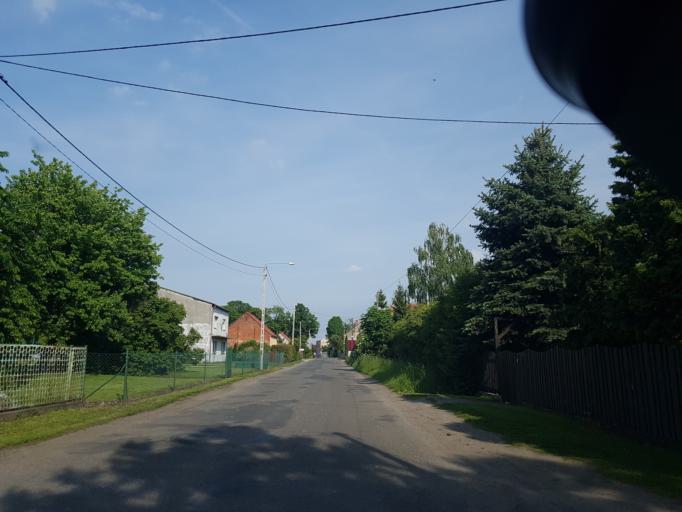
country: PL
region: Lower Silesian Voivodeship
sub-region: Powiat olawski
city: Wierzbno
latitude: 50.9096
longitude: 17.1200
